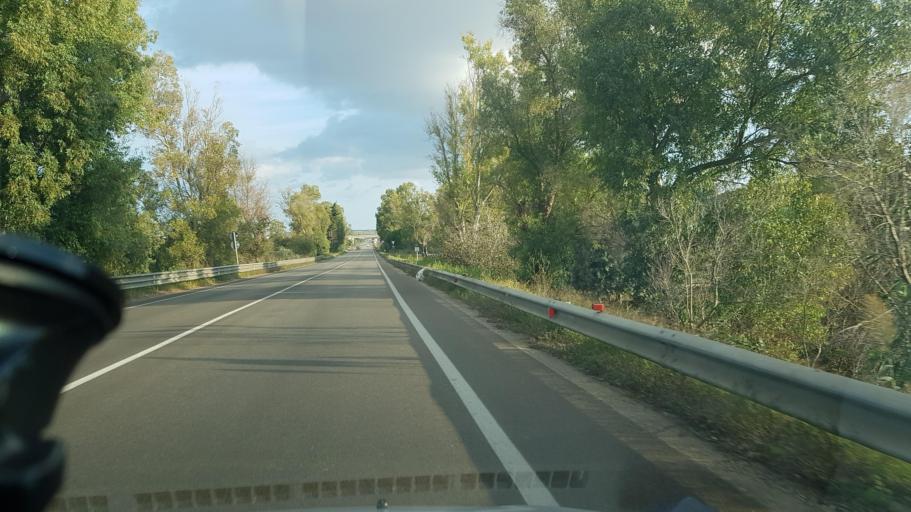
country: IT
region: Apulia
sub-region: Provincia di Lecce
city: Acquarica del Capo
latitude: 39.9040
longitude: 18.2451
